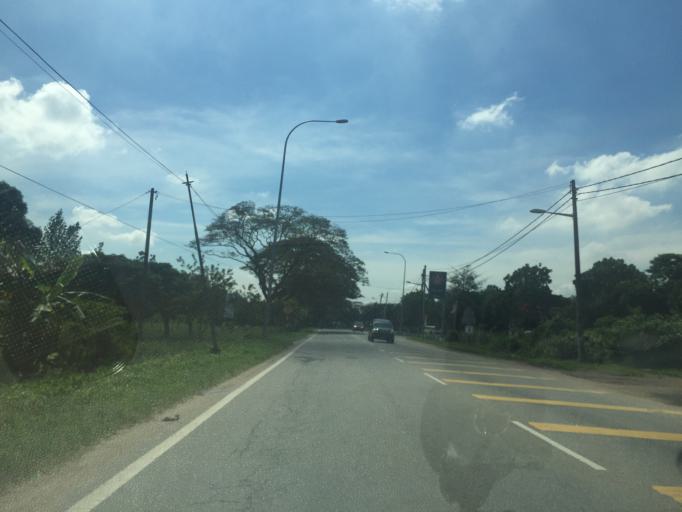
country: MY
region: Penang
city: Tasek Glugor
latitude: 5.4819
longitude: 100.5041
